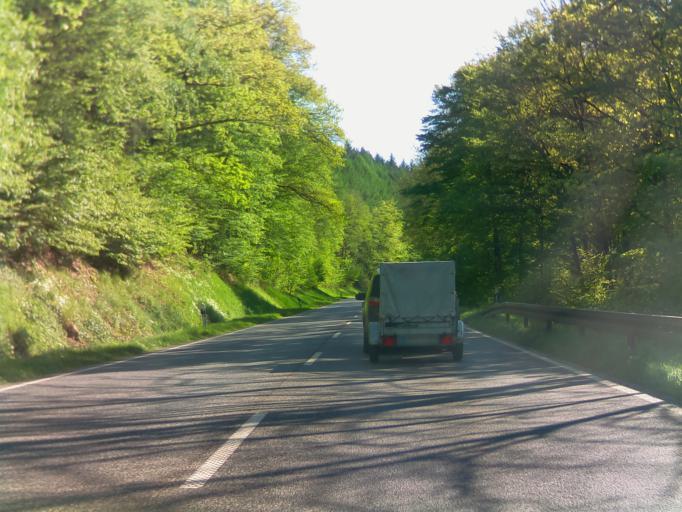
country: DE
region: Hesse
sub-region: Regierungsbezirk Darmstadt
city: Wachtersbach
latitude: 50.2499
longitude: 9.3006
